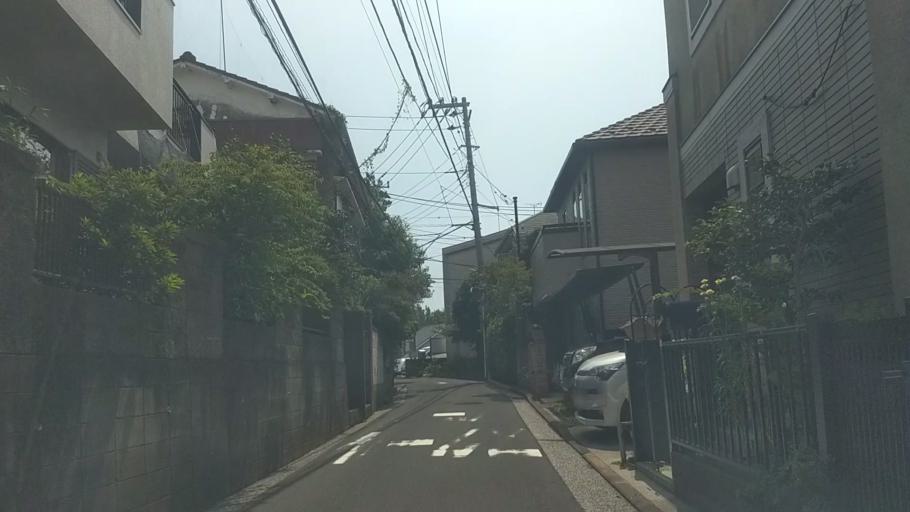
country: JP
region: Kanagawa
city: Yokohama
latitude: 35.5098
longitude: 139.6512
